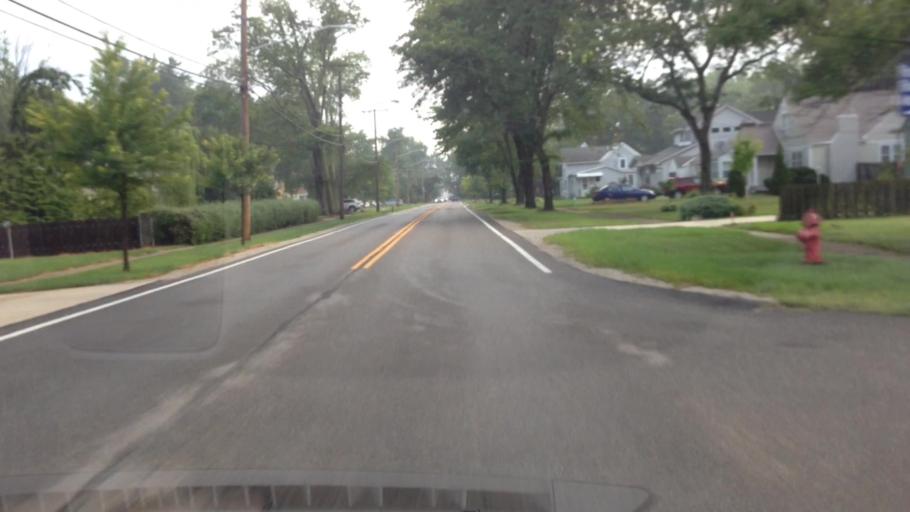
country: US
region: Ohio
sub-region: Cuyahoga County
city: Berea
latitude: 41.3623
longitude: -81.8443
